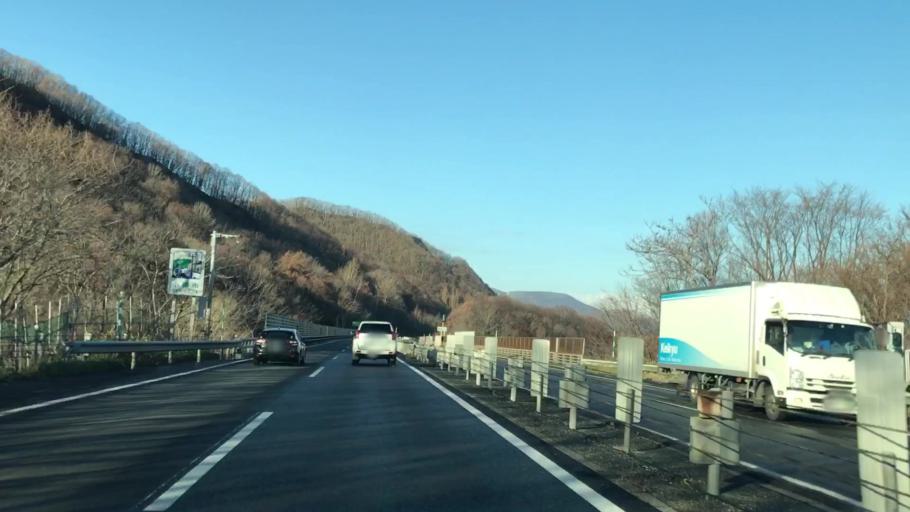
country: JP
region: Hokkaido
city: Sapporo
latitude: 43.1258
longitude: 141.2014
